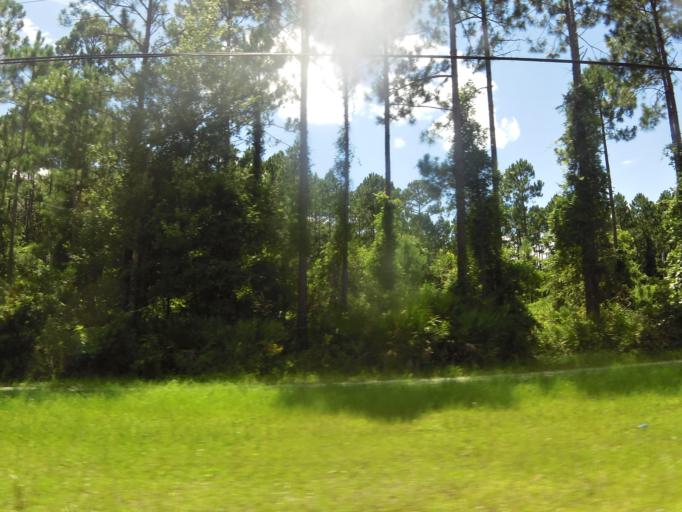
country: US
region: Florida
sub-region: Nassau County
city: Fernandina Beach
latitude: 30.6490
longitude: -81.5302
